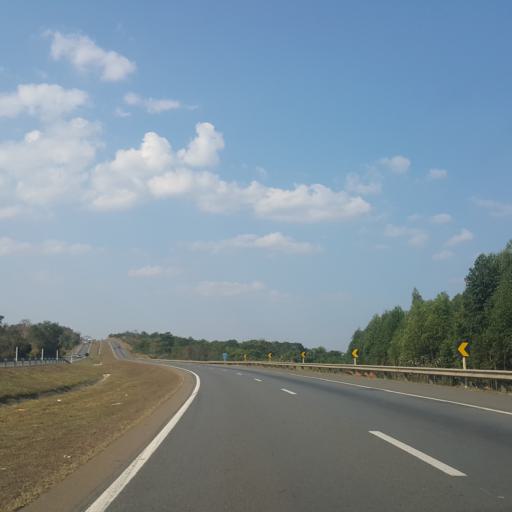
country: BR
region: Goias
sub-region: Abadiania
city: Abadiania
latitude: -16.1706
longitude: -48.6409
